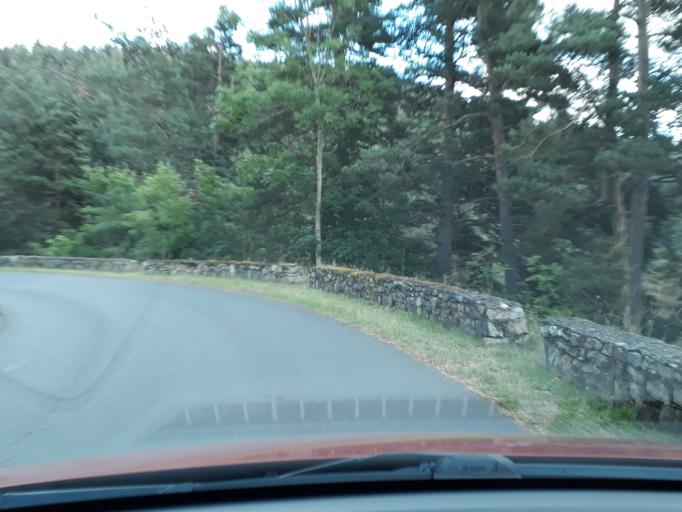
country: FR
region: Auvergne
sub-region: Departement de la Haute-Loire
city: Le Monastier-sur-Gazeille
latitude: 44.8212
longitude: 3.9424
